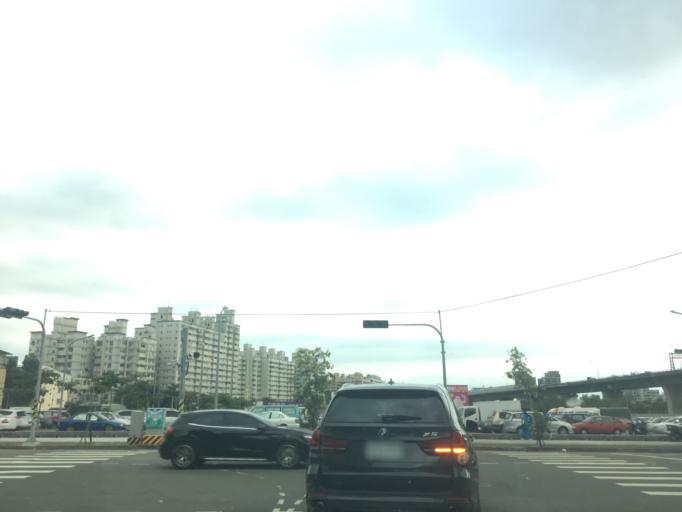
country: TW
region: Taiwan
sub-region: Taichung City
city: Taichung
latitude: 24.1583
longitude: 120.7189
